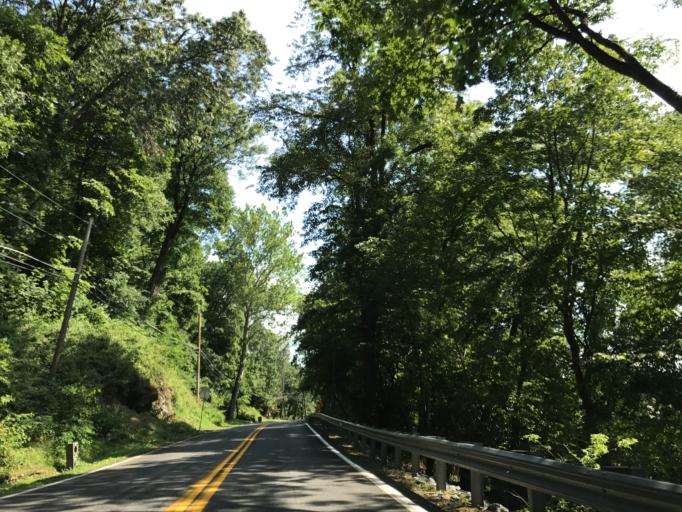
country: US
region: Pennsylvania
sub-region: Lancaster County
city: Conestoga
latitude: 39.8813
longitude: -76.3703
